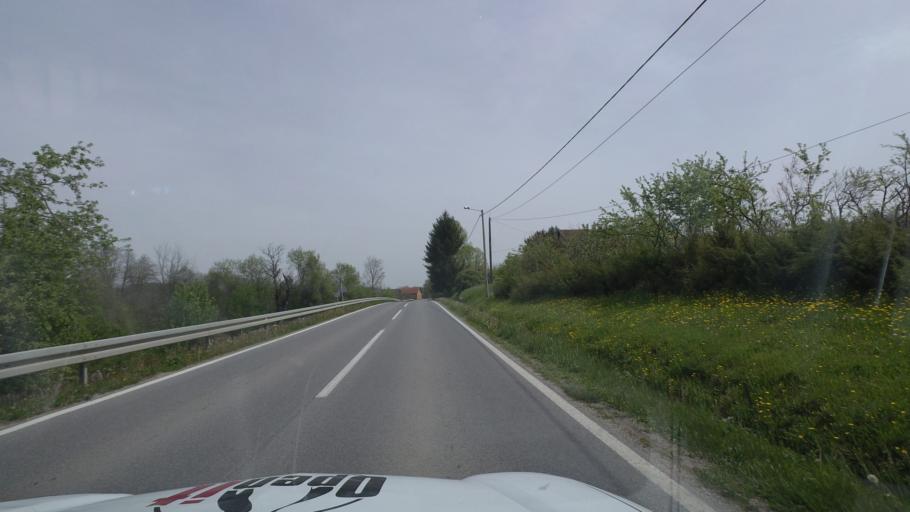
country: HR
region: Sisacko-Moslavacka
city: Petrinja
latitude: 45.4180
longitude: 16.1981
